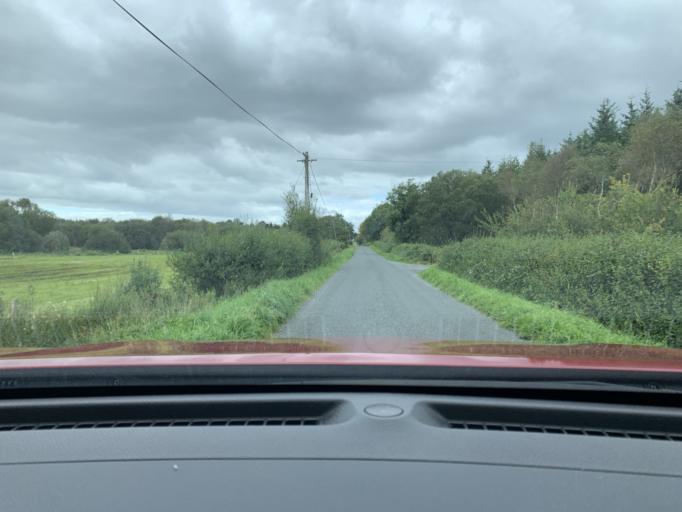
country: IE
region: Connaught
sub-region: Sligo
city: Collooney
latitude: 54.1704
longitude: -8.4353
